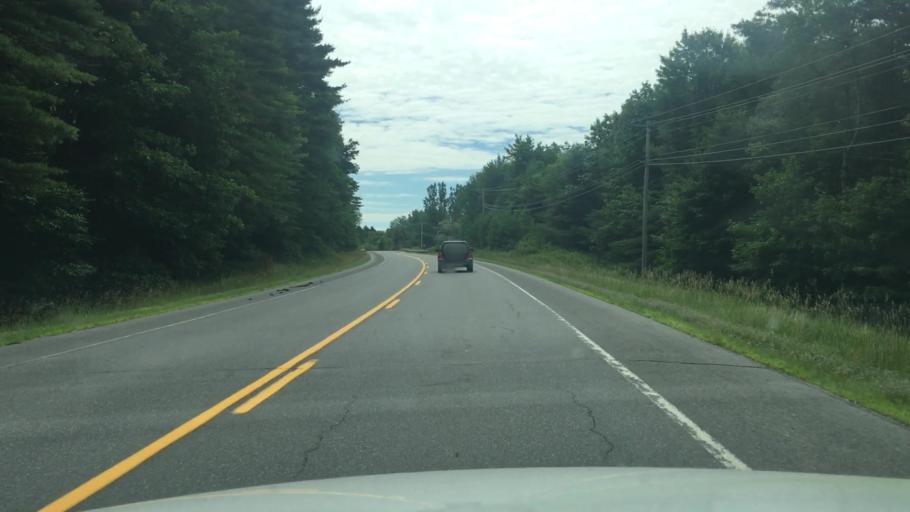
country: US
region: Maine
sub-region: Waldo County
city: Troy
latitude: 44.6126
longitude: -69.3154
